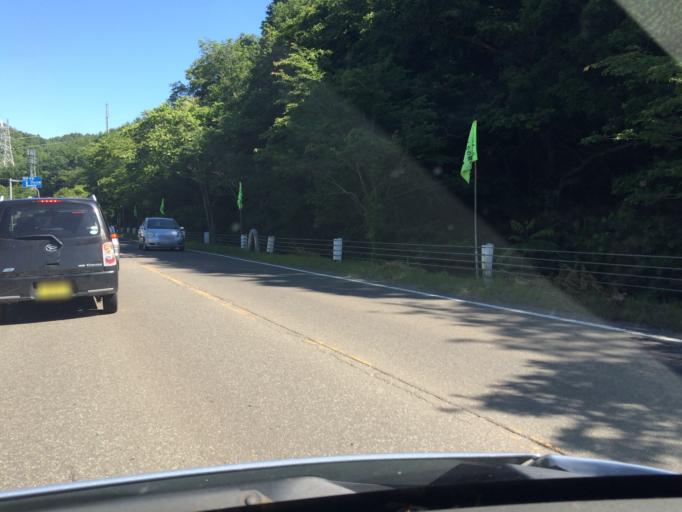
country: JP
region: Hokkaido
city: Sapporo
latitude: 43.0267
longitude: 141.2895
